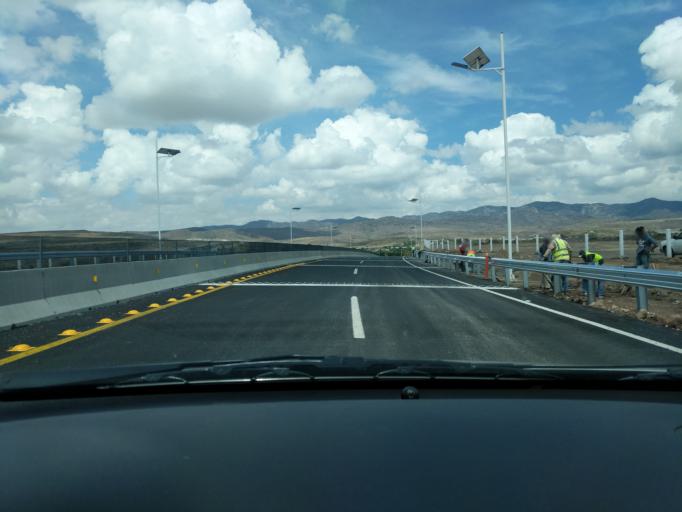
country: MX
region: San Luis Potosi
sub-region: Mexquitic de Carmona
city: Guadalupe Victoria
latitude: 22.1644
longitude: -101.0569
